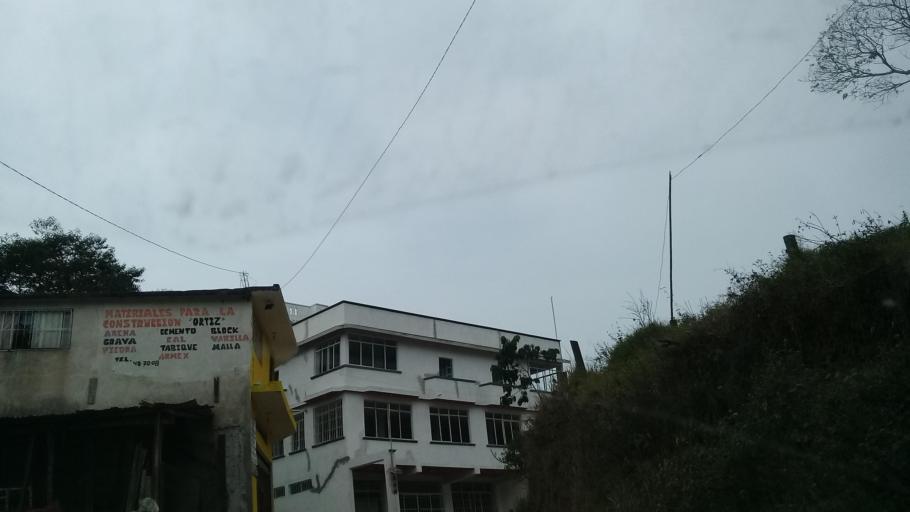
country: MX
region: Veracruz
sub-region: Xalapa
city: Fraccionamiento las Fuentes
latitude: 19.4933
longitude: -96.8987
